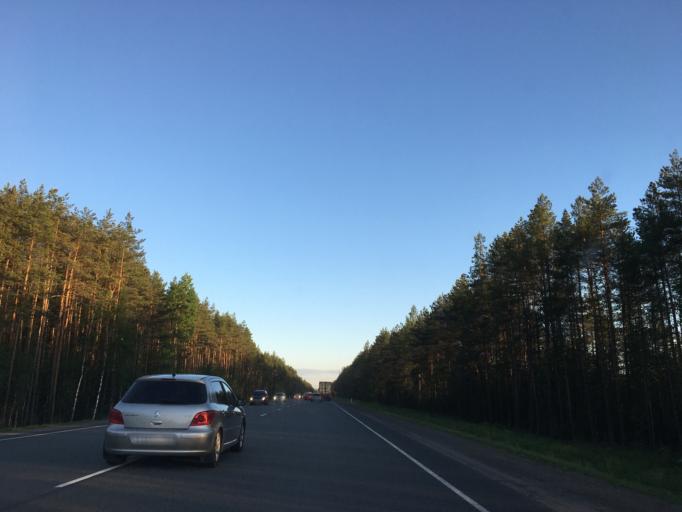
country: RU
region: Leningrad
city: Rozhdestveno
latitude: 59.2957
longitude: 29.9406
